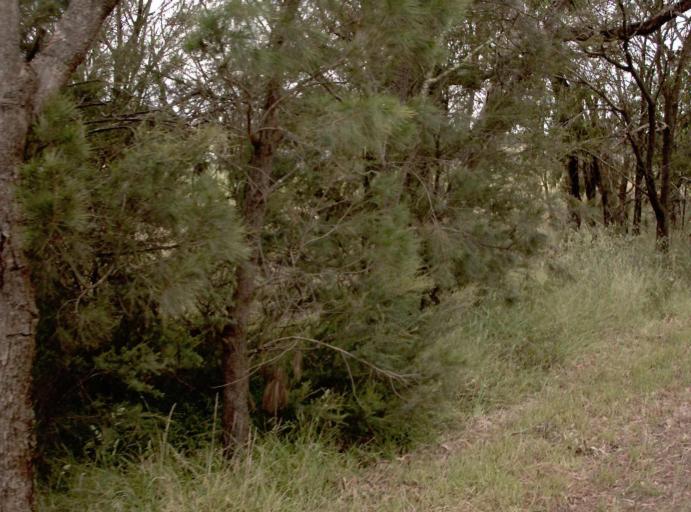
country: AU
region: Victoria
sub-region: Wellington
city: Sale
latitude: -37.9831
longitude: 147.1774
